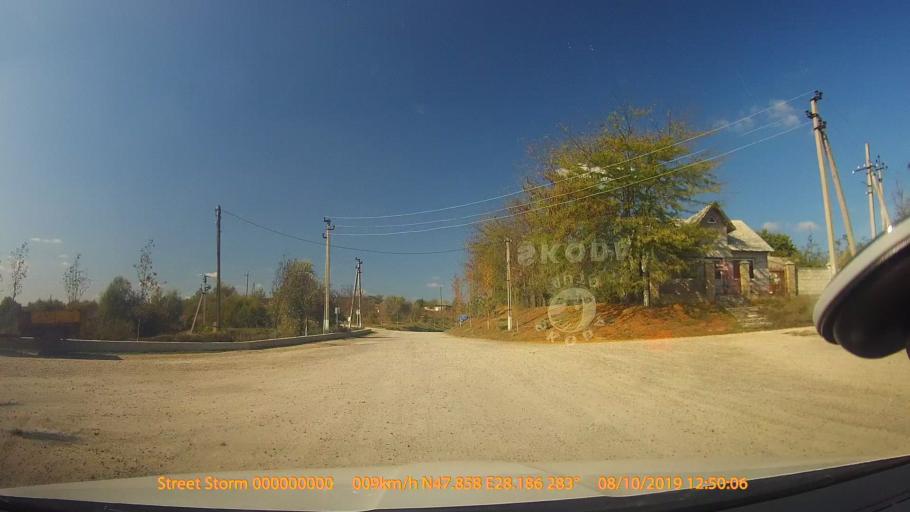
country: MD
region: Floresti
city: Marculesti
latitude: 47.8579
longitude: 28.1864
